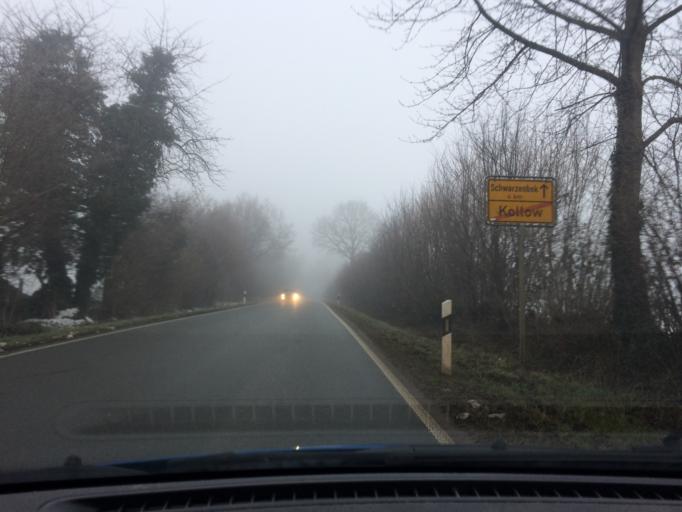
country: DE
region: Schleswig-Holstein
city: Kollow
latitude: 53.4713
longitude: 10.4627
